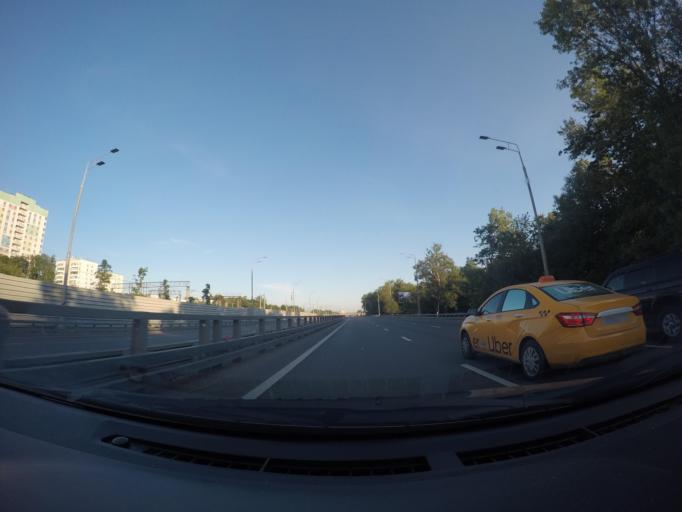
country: RU
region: Moscow
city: Veshnyaki
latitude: 55.7209
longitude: 37.8046
